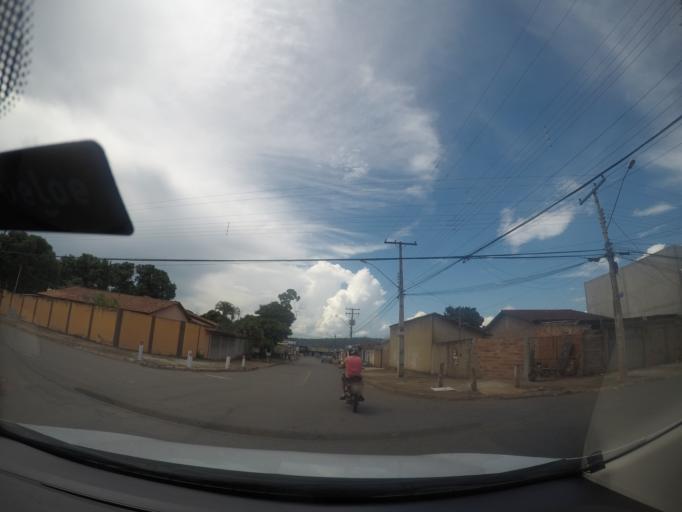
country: BR
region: Goias
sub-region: Goiania
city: Goiania
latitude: -16.6974
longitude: -49.3561
